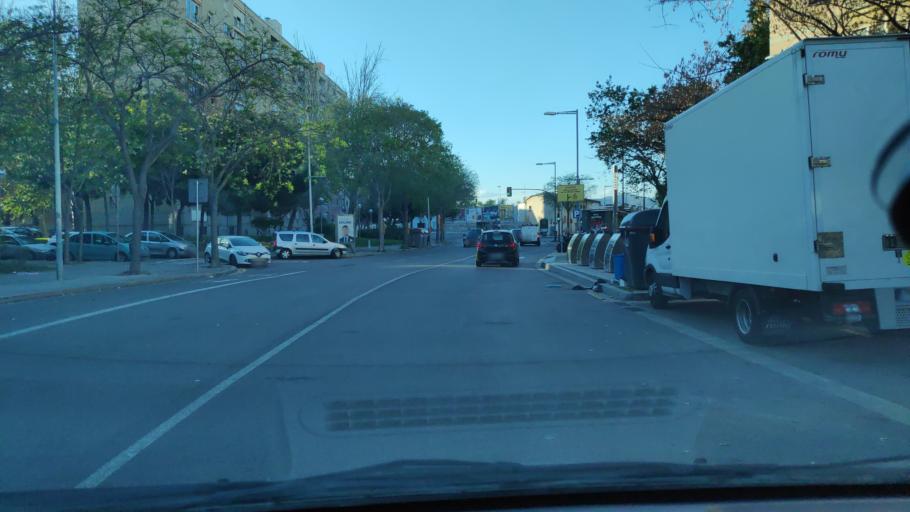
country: ES
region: Catalonia
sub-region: Provincia de Barcelona
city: Sant Adria de Besos
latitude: 41.4225
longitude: 2.2114
